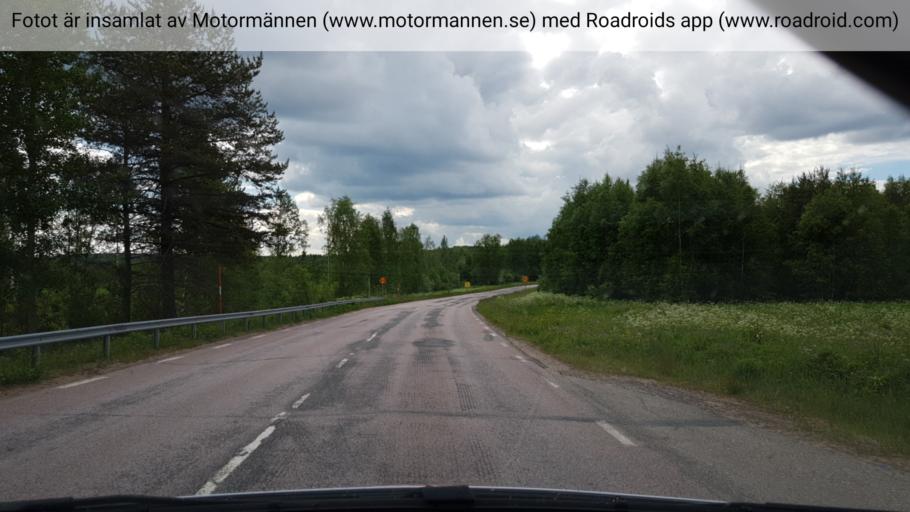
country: FI
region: Lapland
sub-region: Torniolaakso
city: Ylitornio
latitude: 66.2159
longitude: 23.6967
